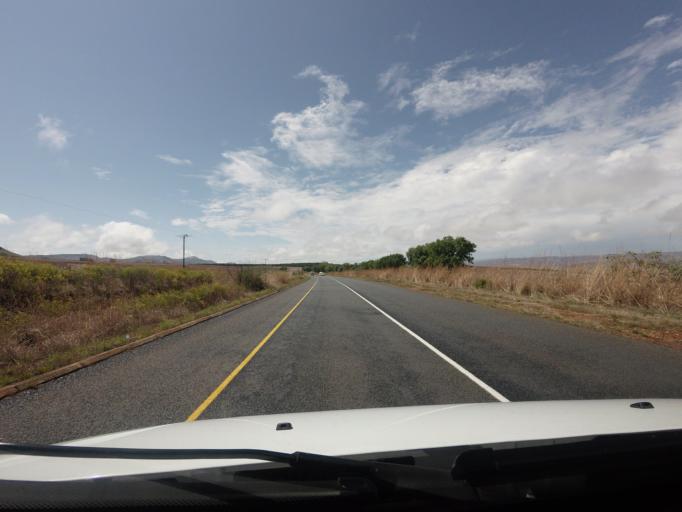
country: ZA
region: Mpumalanga
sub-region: Ehlanzeni District
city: Lydenburg
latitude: -25.1998
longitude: 30.3556
